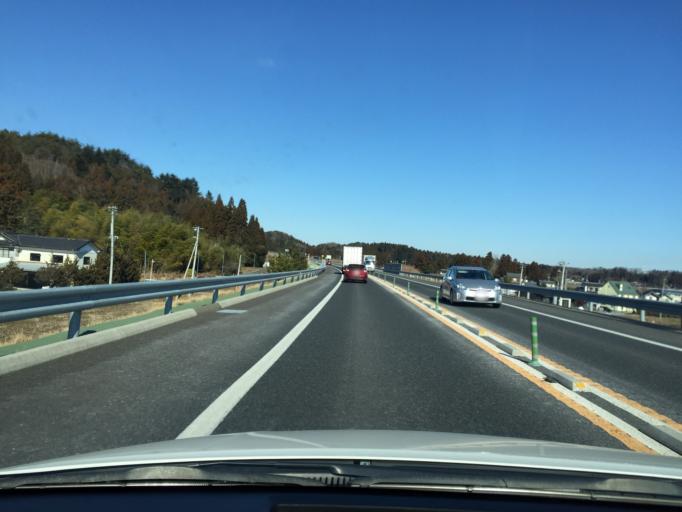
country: JP
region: Miyagi
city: Marumori
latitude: 37.7256
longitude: 140.9167
